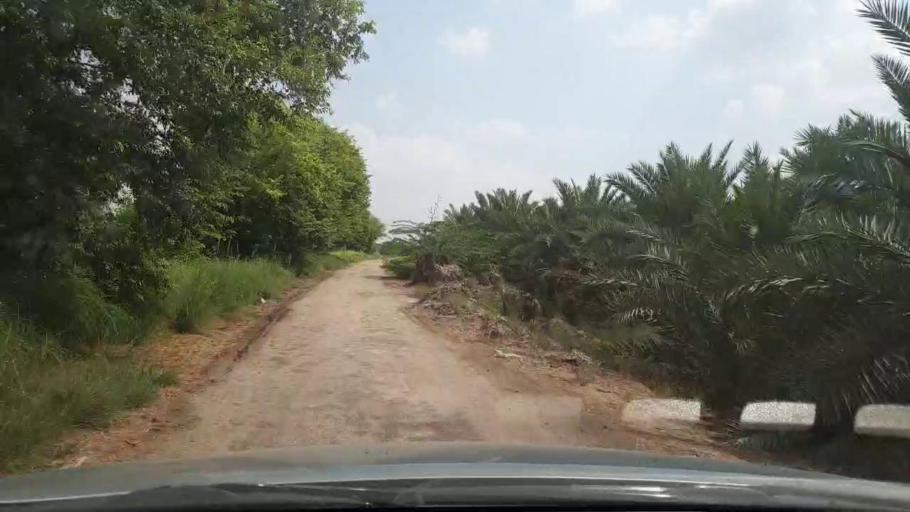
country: PK
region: Sindh
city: Khairpur
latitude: 27.4641
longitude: 68.7773
